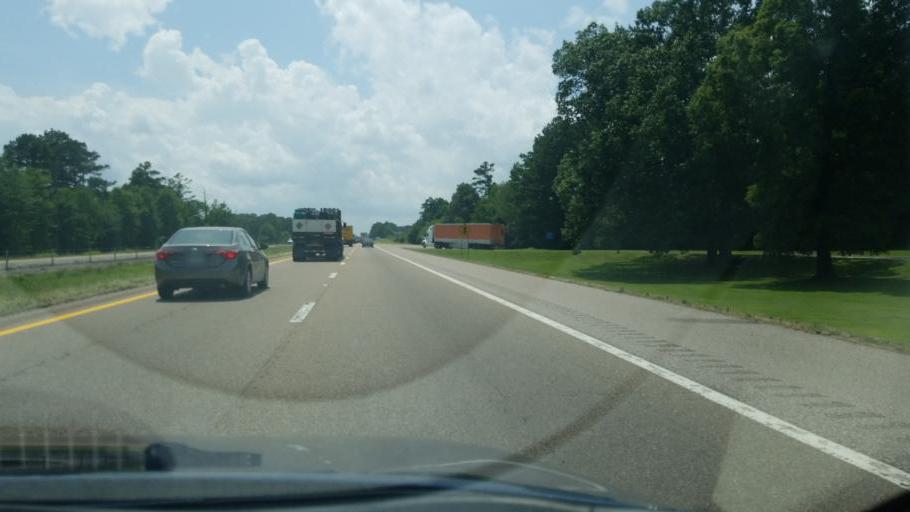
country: US
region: Tennessee
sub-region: Crockett County
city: Bells
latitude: 35.6274
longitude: -88.9683
